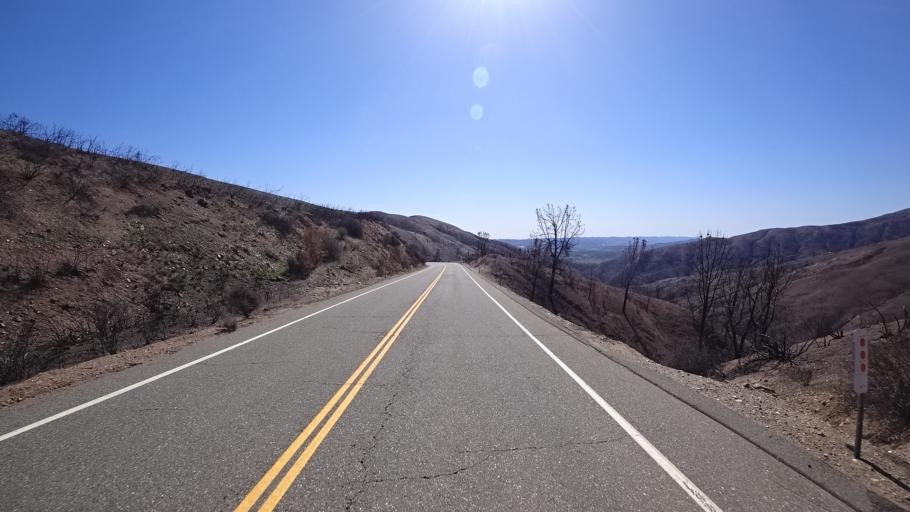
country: US
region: California
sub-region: Tehama County
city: Rancho Tehama Reserve
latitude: 39.6587
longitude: -122.6264
